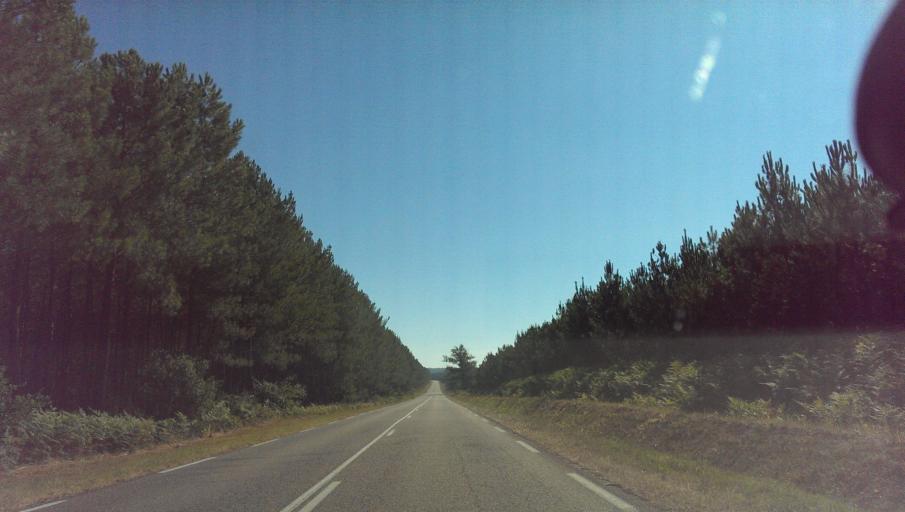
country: FR
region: Aquitaine
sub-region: Departement du Lot-et-Garonne
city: Barbaste
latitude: 44.2153
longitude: 0.1965
